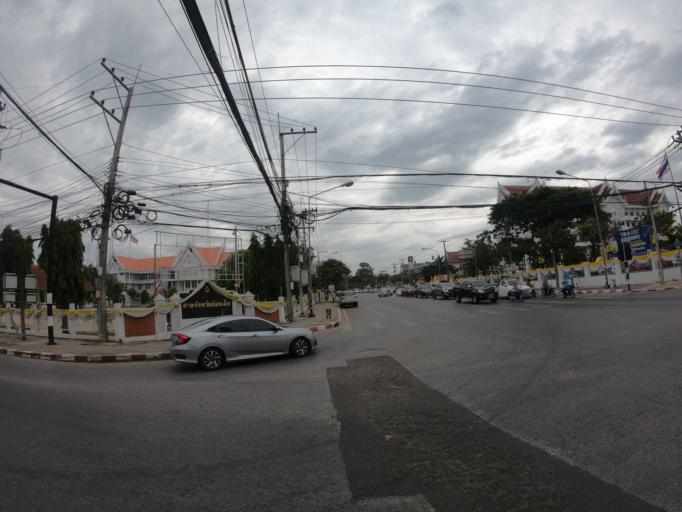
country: TH
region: Roi Et
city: Roi Et
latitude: 16.0538
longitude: 103.6533
